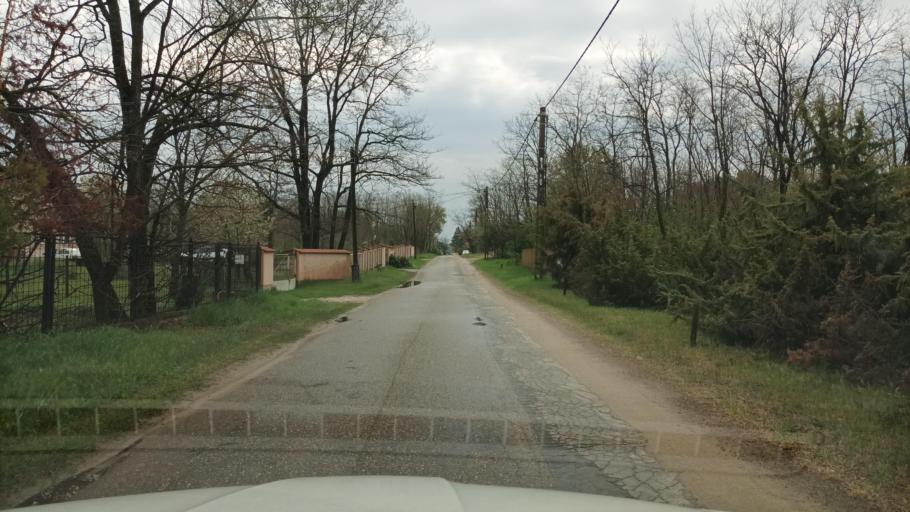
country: HU
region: Pest
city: Hernad
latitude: 47.1803
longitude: 19.4612
